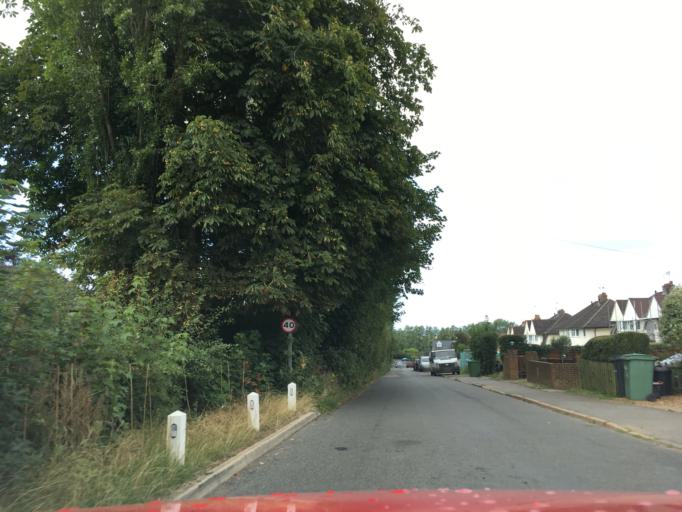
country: GB
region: England
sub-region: Kent
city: Maidstone
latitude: 51.2322
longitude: 0.5210
